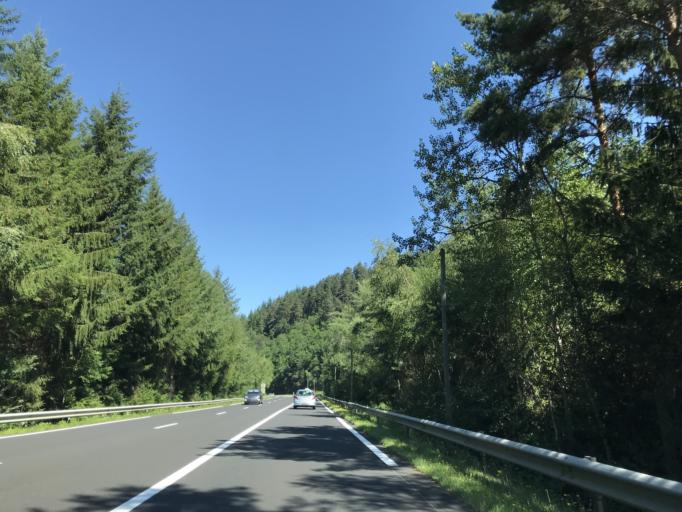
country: FR
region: Auvergne
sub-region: Departement du Puy-de-Dome
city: Job
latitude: 45.6084
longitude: 3.7207
